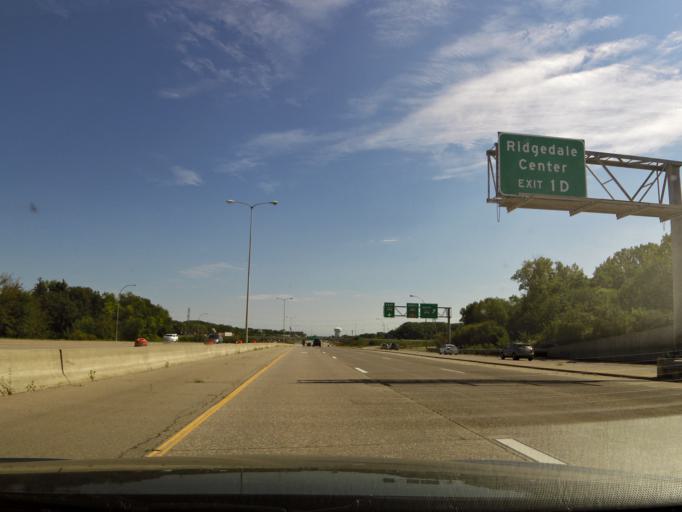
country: US
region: Minnesota
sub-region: Hennepin County
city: Minnetonka Mills
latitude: 44.9710
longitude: -93.4673
